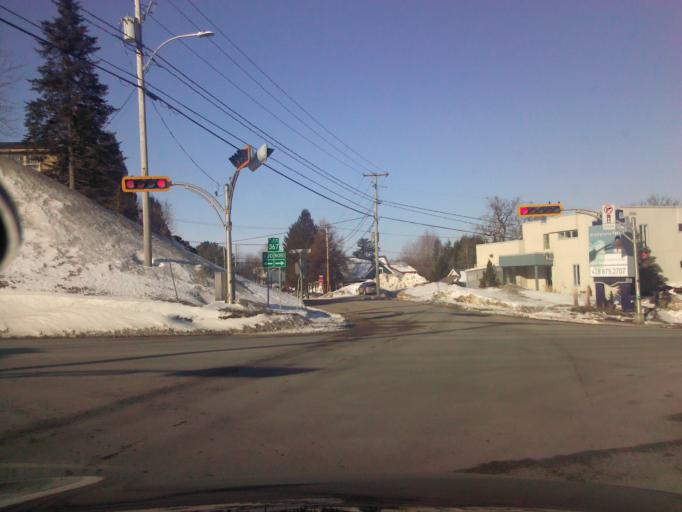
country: CA
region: Quebec
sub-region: Capitale-Nationale
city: Sainte Catherine de la Jacques Cartier
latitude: 46.8445
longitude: -71.6150
